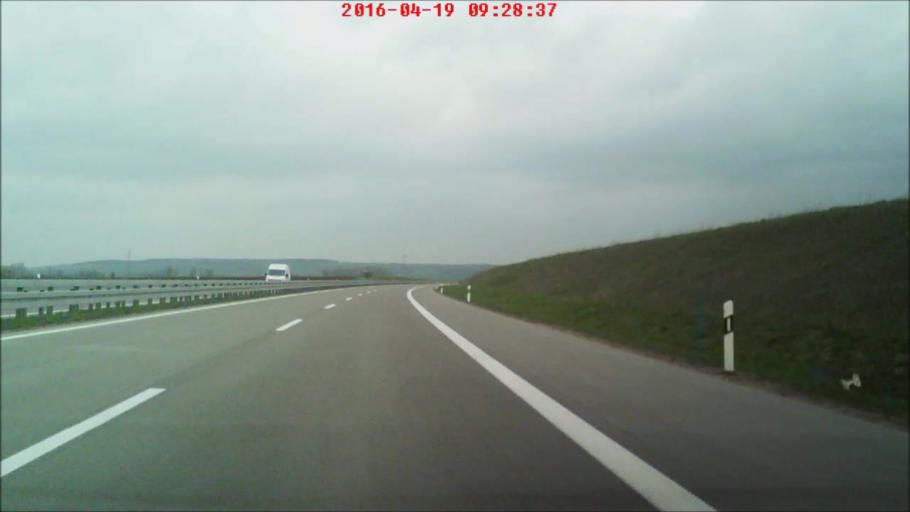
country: DE
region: Thuringia
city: Schillingstedt
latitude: 51.2344
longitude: 11.1831
